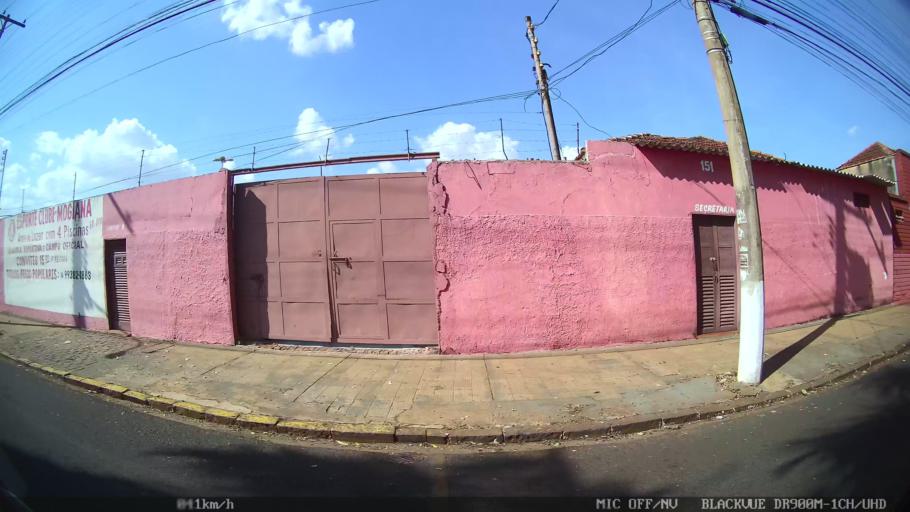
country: BR
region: Sao Paulo
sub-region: Ribeirao Preto
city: Ribeirao Preto
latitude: -21.1798
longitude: -47.8224
